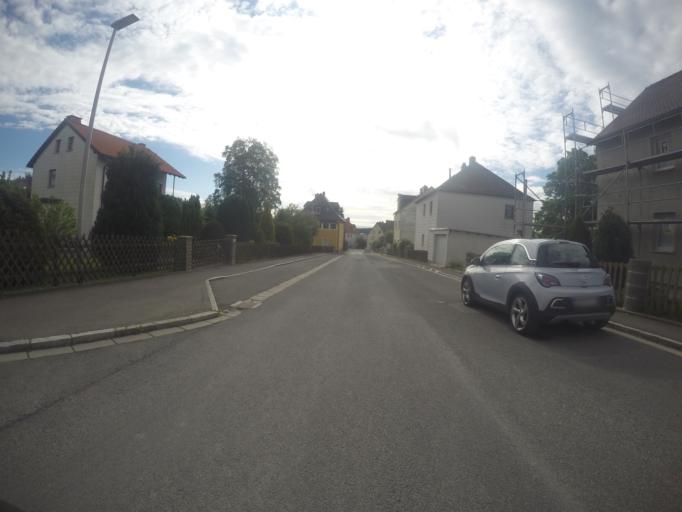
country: DE
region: Bavaria
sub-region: Upper Franconia
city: Schonwald
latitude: 50.2009
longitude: 12.0920
